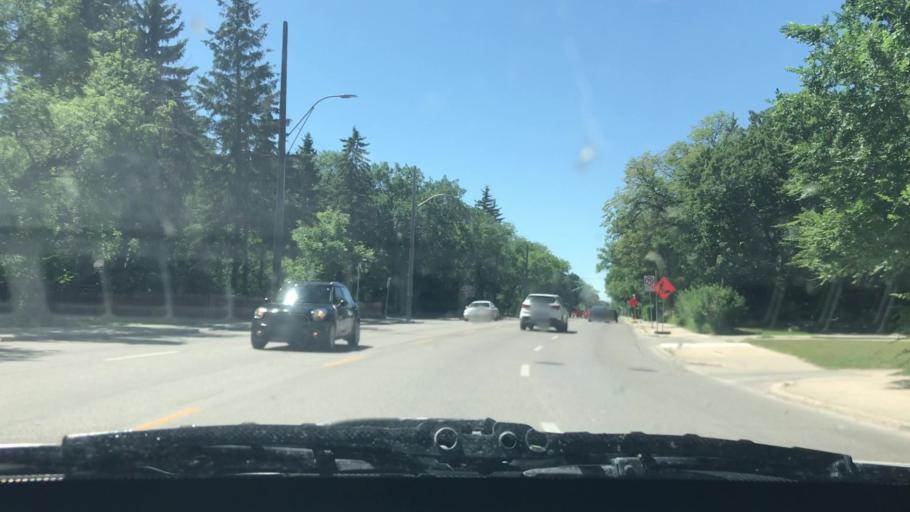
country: CA
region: Manitoba
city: Winnipeg
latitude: 49.8735
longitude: -97.1718
